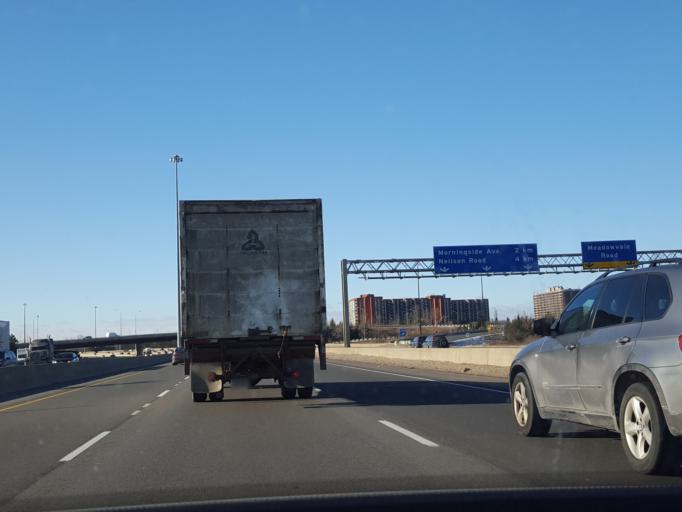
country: CA
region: Ontario
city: Scarborough
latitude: 43.7981
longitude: -79.1614
